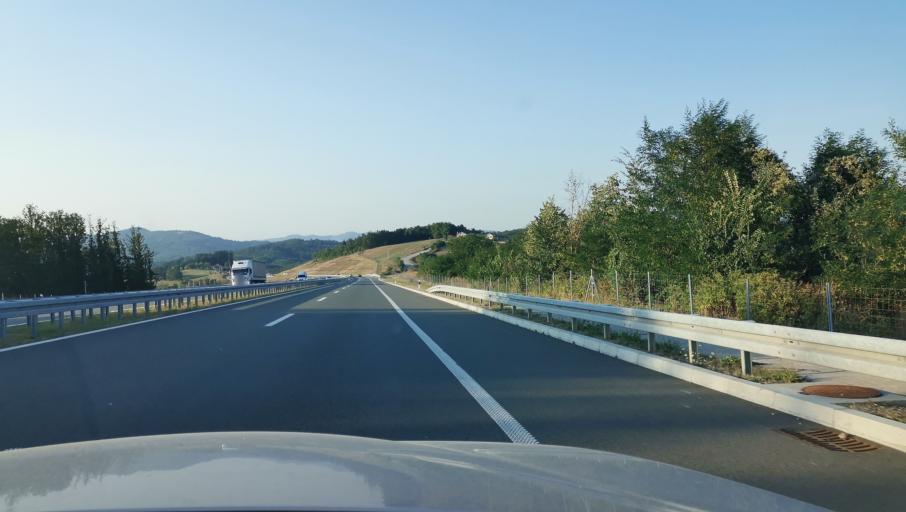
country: RS
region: Central Serbia
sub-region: Moravicki Okrug
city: Gornji Milanovac
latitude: 44.1009
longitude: 20.3843
